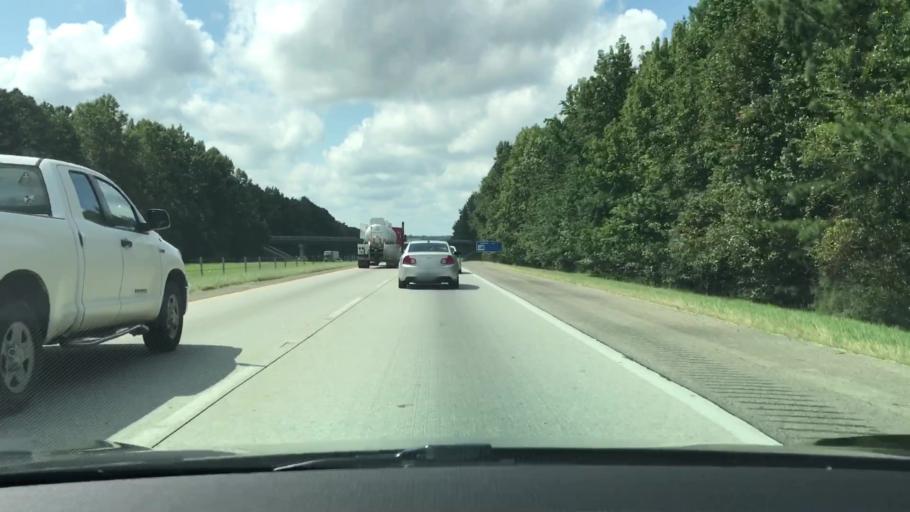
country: US
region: Georgia
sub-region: Hall County
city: Flowery Branch
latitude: 34.1622
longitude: -83.9266
